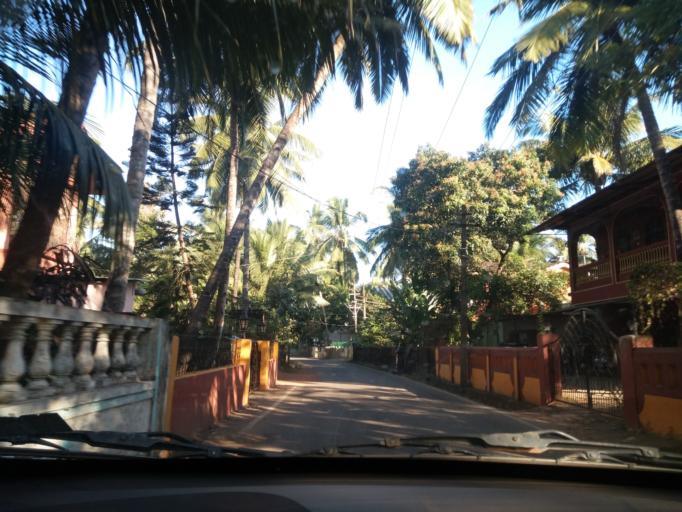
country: IN
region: Goa
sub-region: South Goa
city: Madgaon
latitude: 15.2541
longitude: 73.9560
